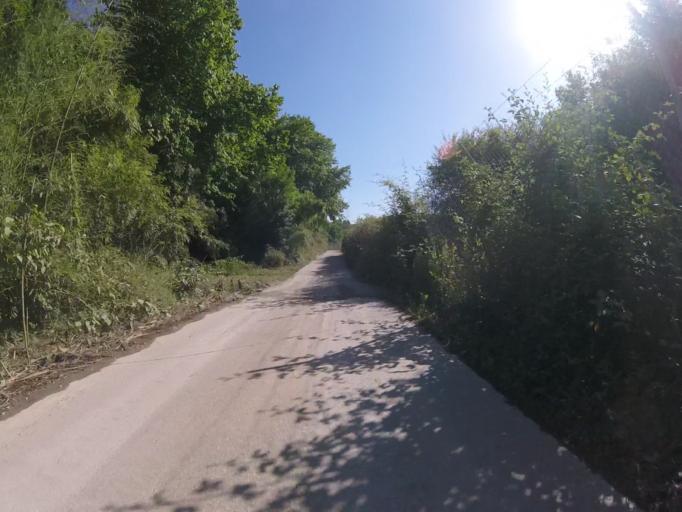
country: ES
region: Basque Country
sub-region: Provincia de Guipuzcoa
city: Astigarraga
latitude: 43.2862
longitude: -1.9526
